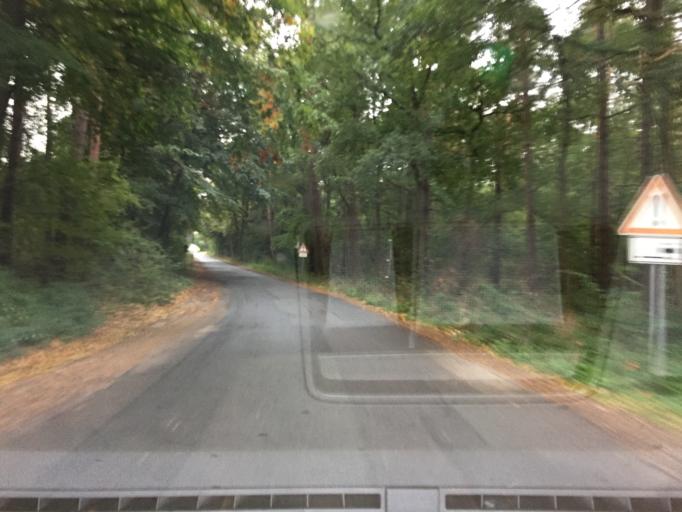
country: DE
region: Lower Saxony
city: Liebenau
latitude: 52.6207
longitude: 9.0934
